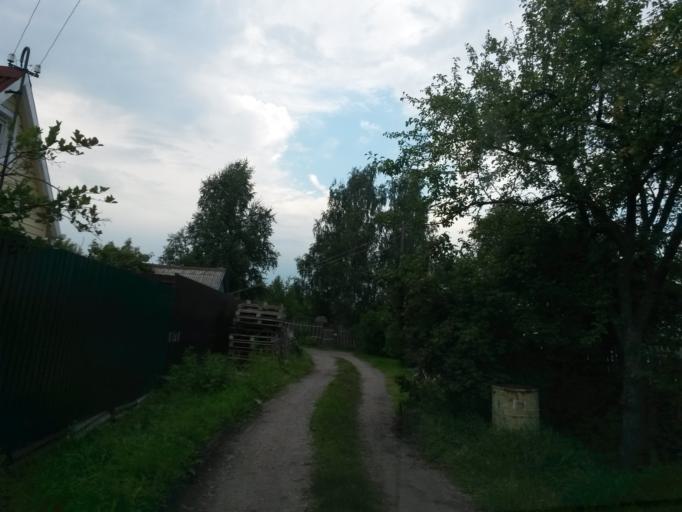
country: RU
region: Jaroslavl
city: Yaroslavl
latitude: 57.6098
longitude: 39.7842
